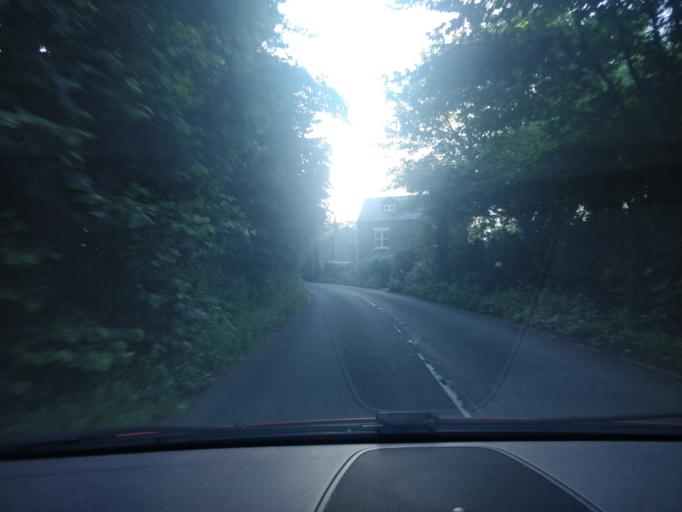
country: GB
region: England
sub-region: Lancashire
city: Skelmersdale
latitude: 53.5525
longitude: -2.7428
